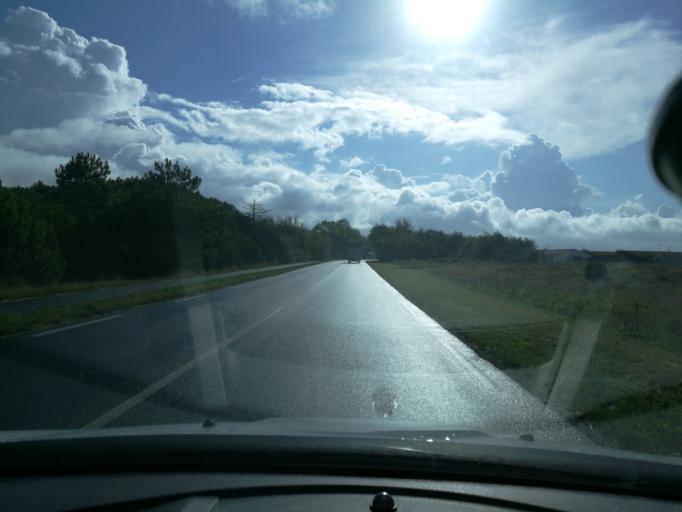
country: FR
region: Poitou-Charentes
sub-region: Departement de la Charente-Maritime
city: Sainte-Marie-de-Re
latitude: 46.1568
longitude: -1.3188
